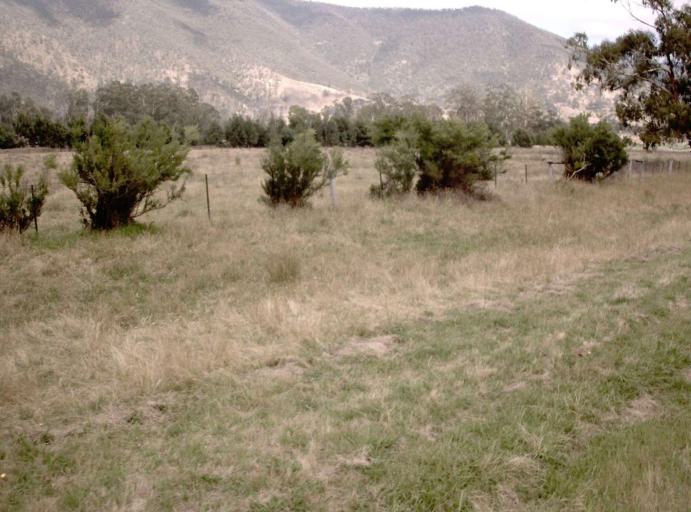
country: AU
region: Victoria
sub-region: Wellington
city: Heyfield
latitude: -37.6415
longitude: 146.6378
